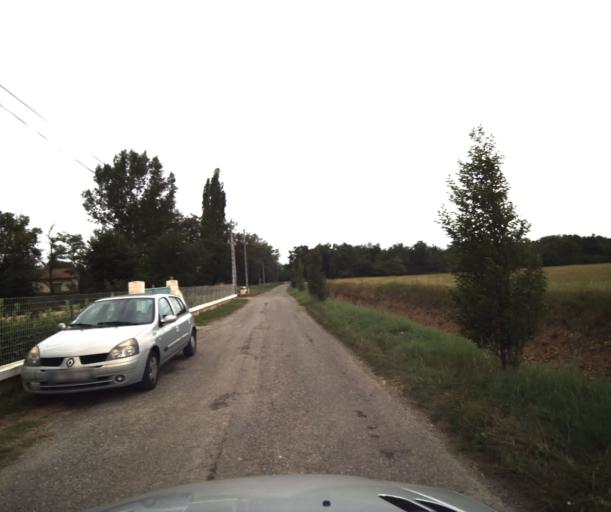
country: FR
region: Midi-Pyrenees
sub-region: Departement de la Haute-Garonne
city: Labarthe-sur-Leze
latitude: 43.4682
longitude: 1.4013
